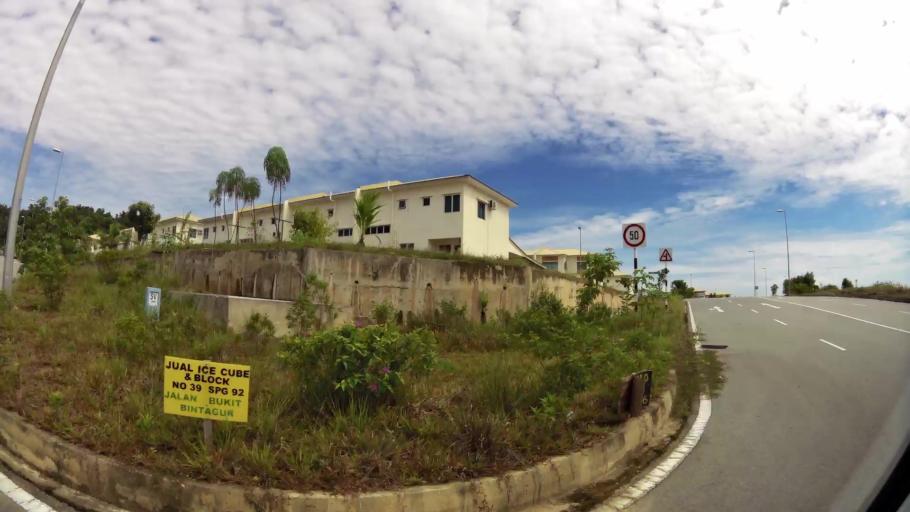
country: BN
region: Brunei and Muara
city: Bandar Seri Begawan
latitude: 4.9815
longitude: 115.0119
